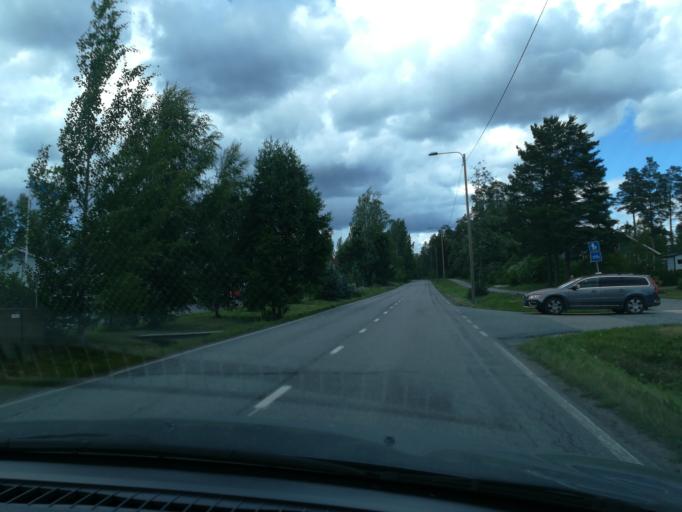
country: FI
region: Southern Savonia
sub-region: Mikkeli
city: Hirvensalmi
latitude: 61.6491
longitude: 26.7715
